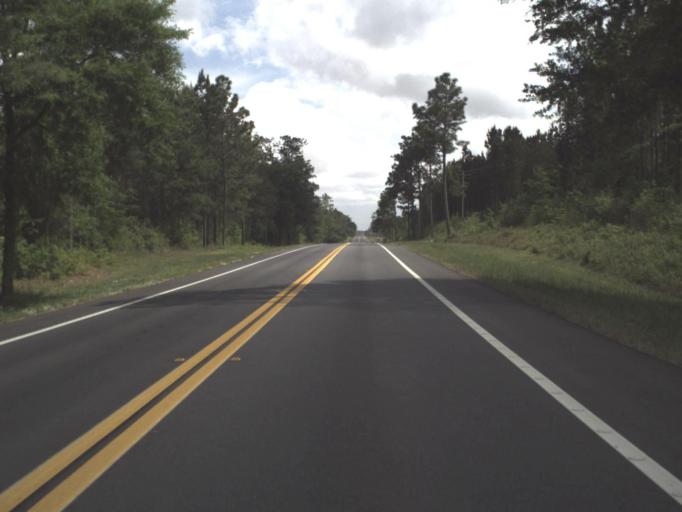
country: US
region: Florida
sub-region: Santa Rosa County
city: Wallace
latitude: 30.8409
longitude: -87.1443
